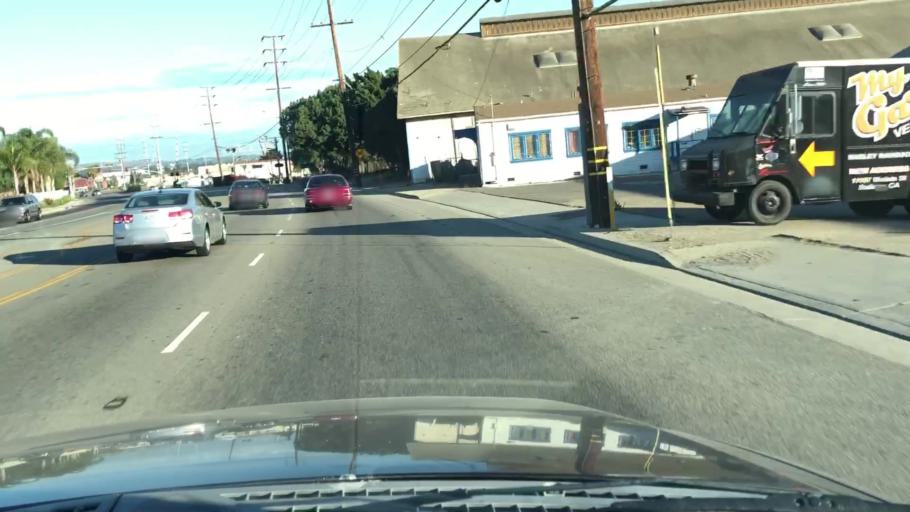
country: US
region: California
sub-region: Ventura County
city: Saticoy
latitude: 34.2827
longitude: -119.1500
